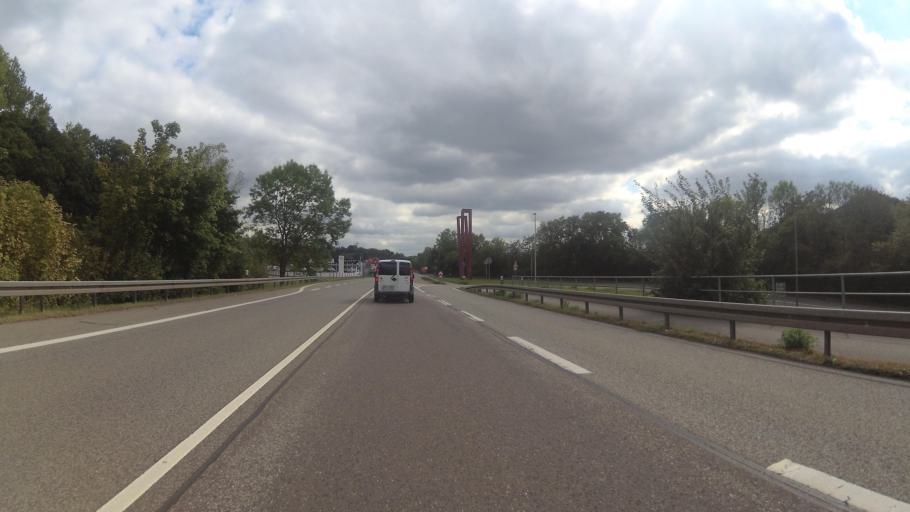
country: DE
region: Saarland
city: Volklingen
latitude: 49.2659
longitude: 6.8349
